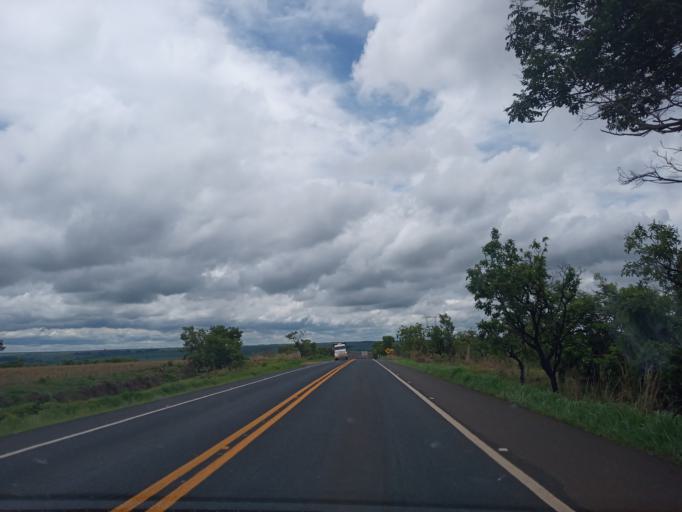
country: BR
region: Minas Gerais
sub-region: Uberaba
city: Uberaba
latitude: -19.2896
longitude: -47.6075
